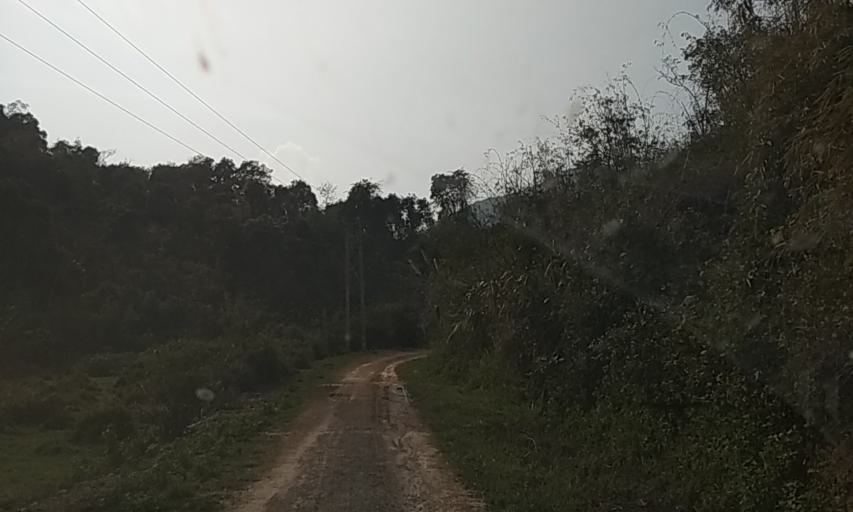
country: LA
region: Louangphabang
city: Louangphabang
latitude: 20.0427
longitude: 101.8074
